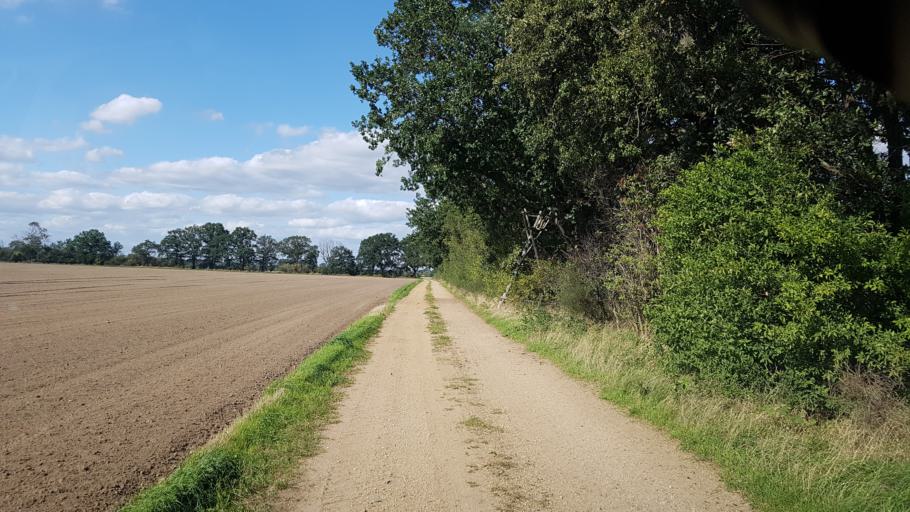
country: DE
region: Brandenburg
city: Sonnewalde
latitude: 51.6859
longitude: 13.6639
